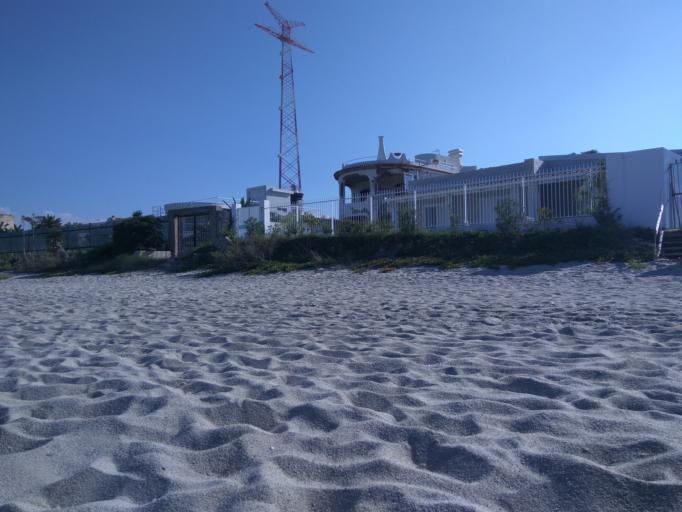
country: IT
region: Calabria
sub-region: Provincia di Reggio Calabria
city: Villa San Giovanni
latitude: 38.2702
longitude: 15.6504
